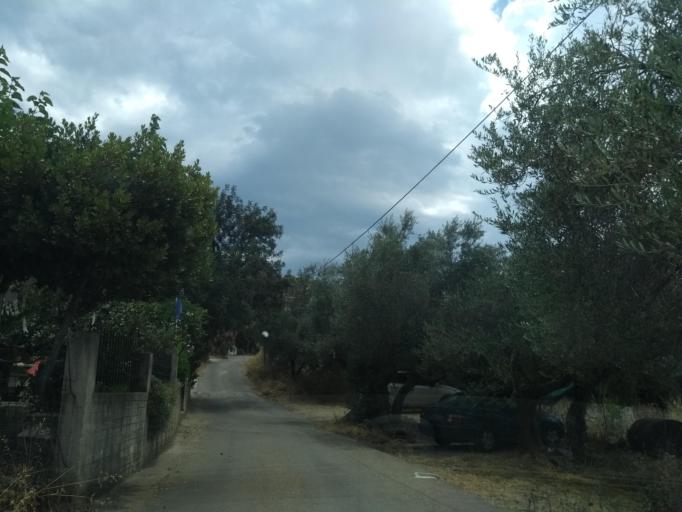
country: GR
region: Crete
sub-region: Nomos Chanias
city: Georgioupolis
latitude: 35.3789
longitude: 24.2447
